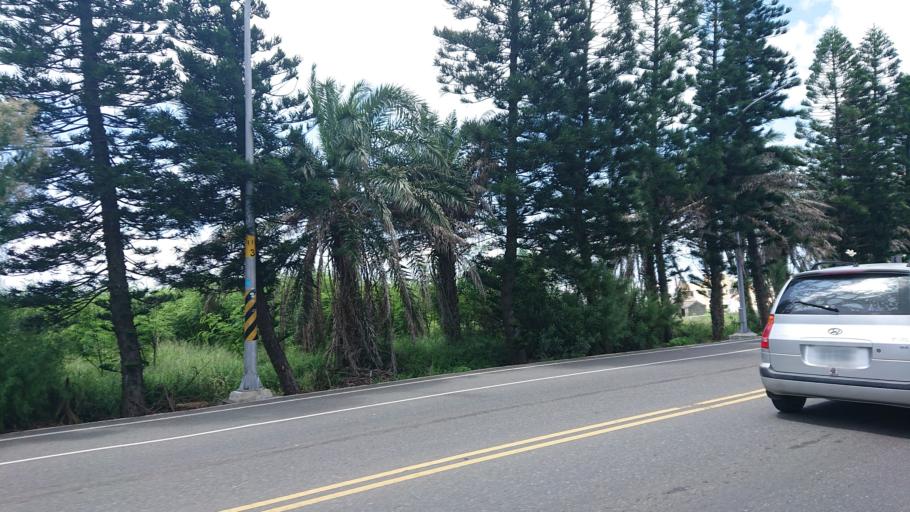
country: TW
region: Taiwan
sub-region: Penghu
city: Ma-kung
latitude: 23.5834
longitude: 119.6073
